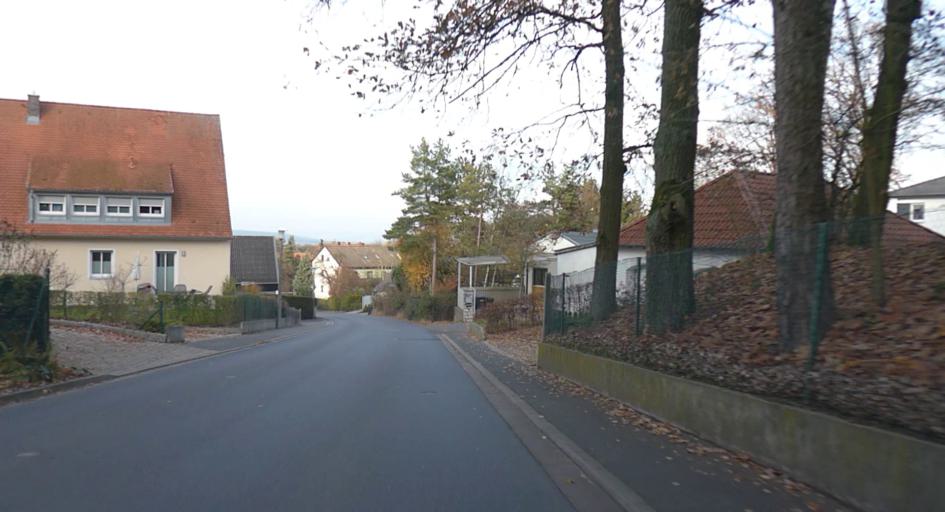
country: DE
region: Bavaria
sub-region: Regierungsbezirk Mittelfranken
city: Bubenreuth
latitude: 49.6294
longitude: 11.0393
